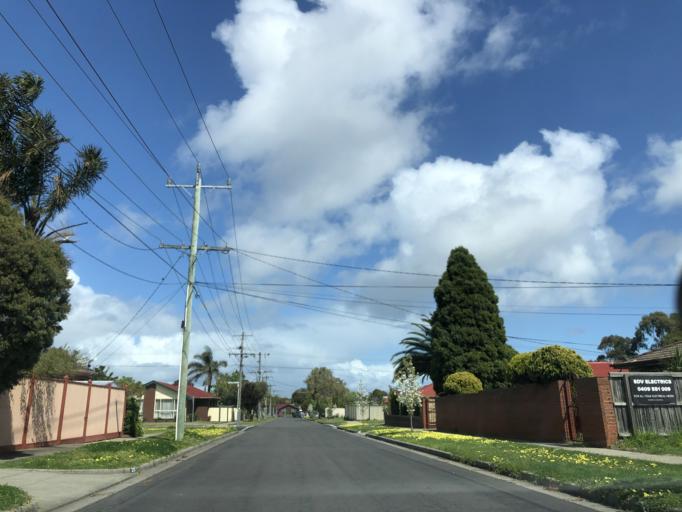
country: AU
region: Victoria
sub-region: Kingston
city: Clayton South
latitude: -37.9426
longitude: 145.1050
